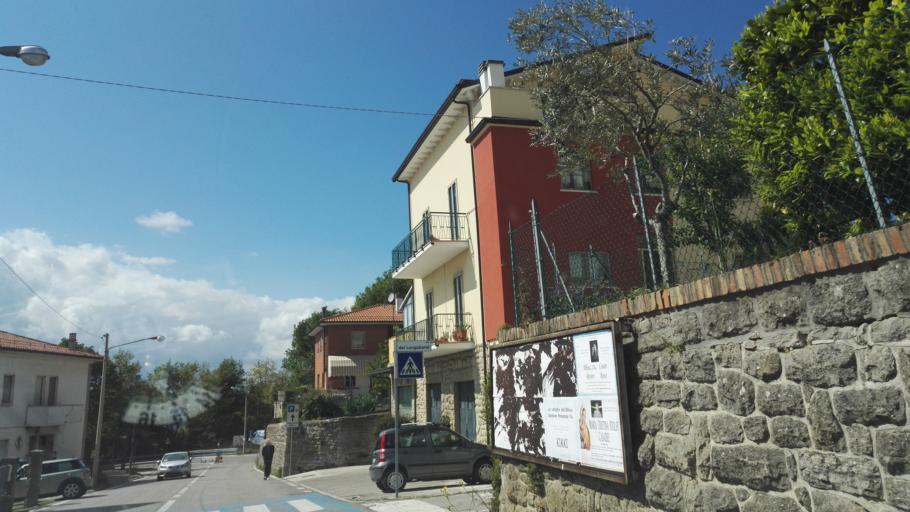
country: SM
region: San Marino
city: San Marino
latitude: 43.9375
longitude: 12.4417
